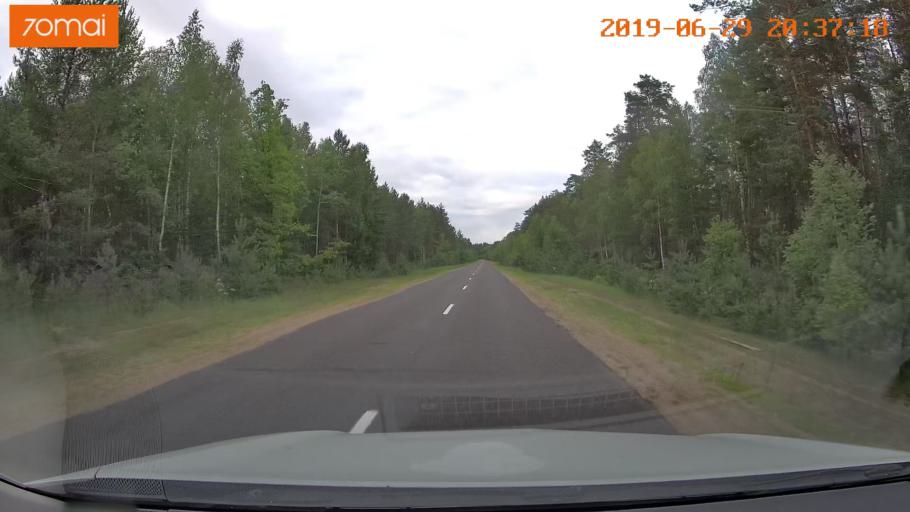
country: BY
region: Brest
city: Hantsavichy
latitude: 52.5363
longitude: 26.3639
